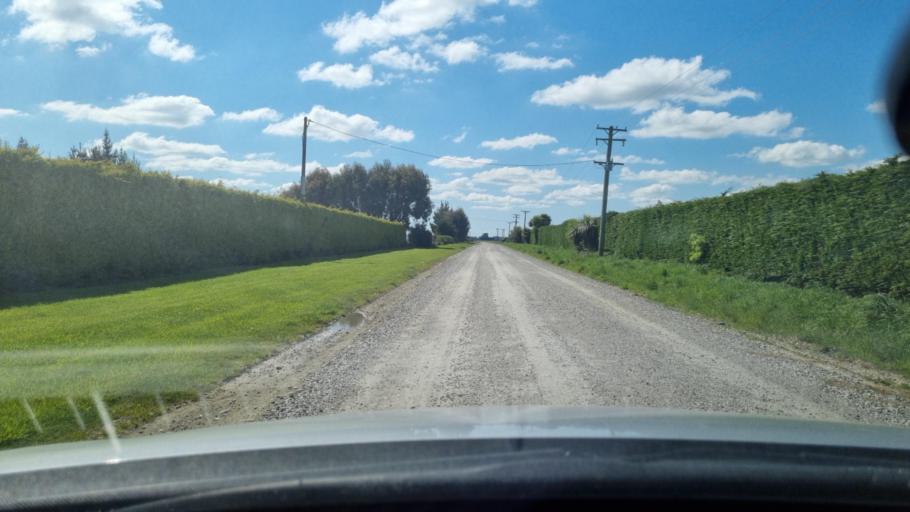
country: NZ
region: Southland
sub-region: Invercargill City
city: Invercargill
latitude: -46.3739
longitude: 168.2985
